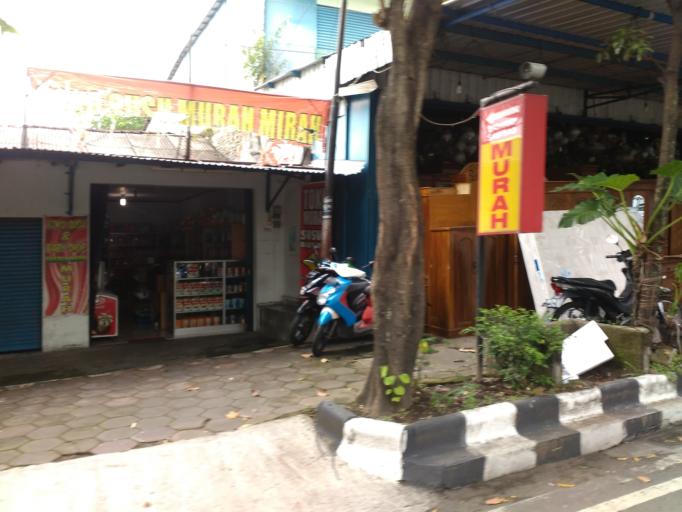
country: ID
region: Central Java
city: Boyolali
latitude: -7.5307
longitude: 110.6017
